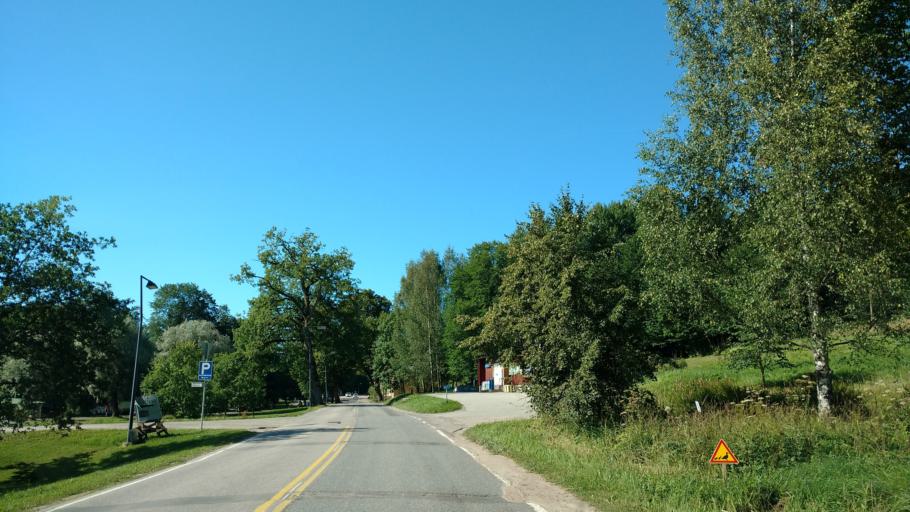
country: FI
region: Uusimaa
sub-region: Raaseporin
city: Pohja
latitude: 60.1317
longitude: 23.5446
